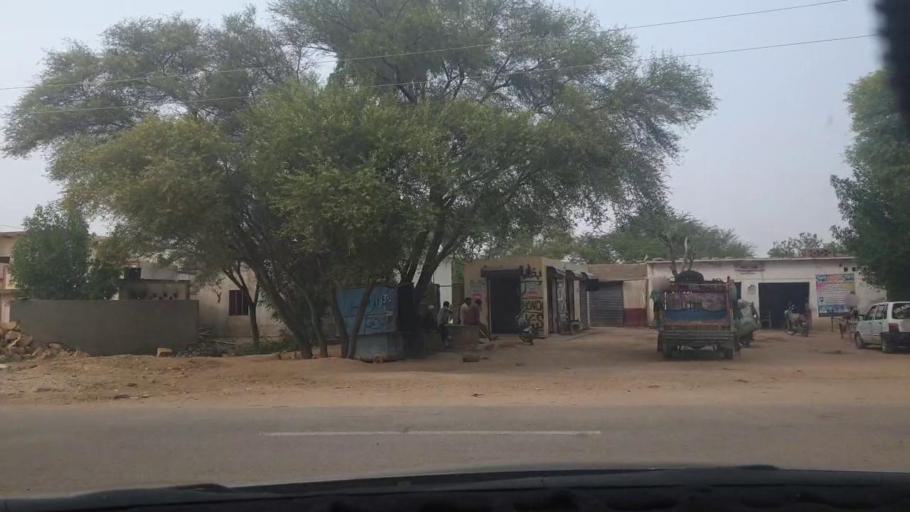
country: PK
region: Sindh
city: Jamshoro
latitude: 25.5174
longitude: 68.2945
